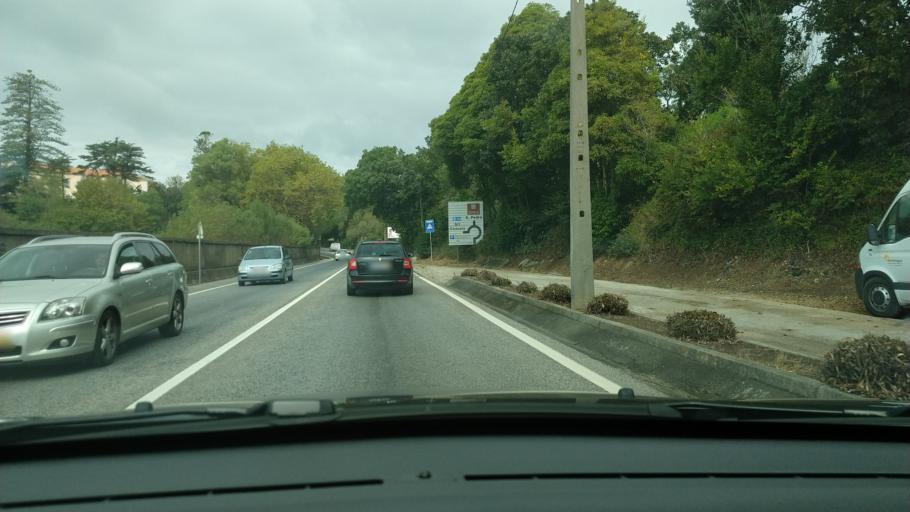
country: PT
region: Lisbon
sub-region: Sintra
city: Sintra
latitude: 38.7846
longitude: -9.3708
